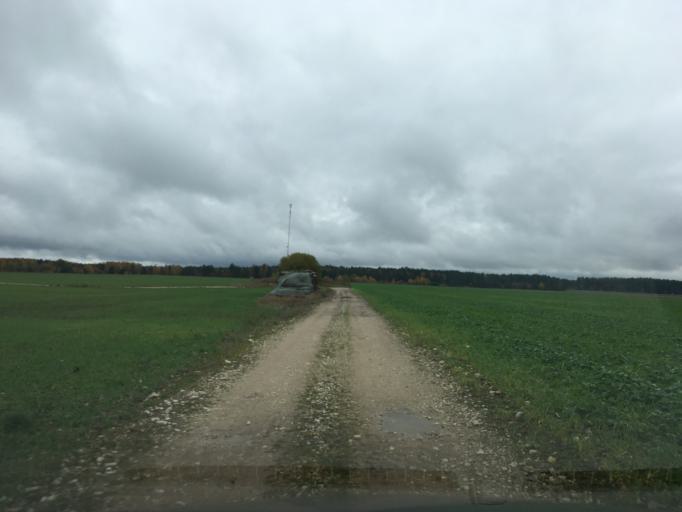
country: EE
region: Harju
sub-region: Raasiku vald
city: Raasiku
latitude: 59.1810
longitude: 25.1513
